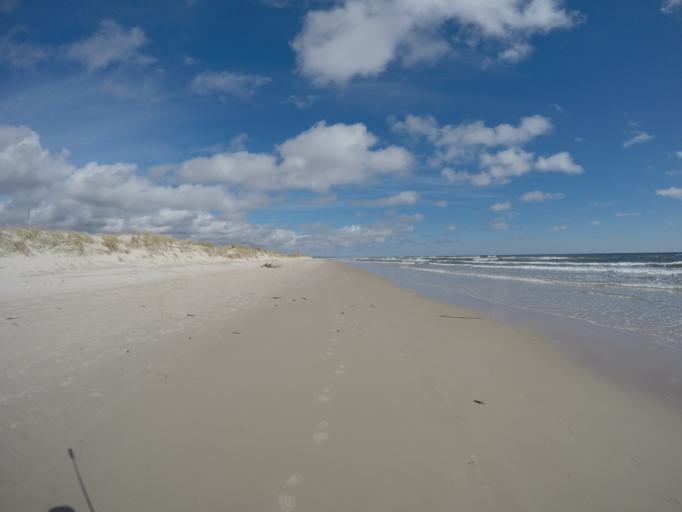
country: SE
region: Skane
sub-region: Simrishamns Kommun
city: Simrishamn
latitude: 55.3917
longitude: 14.2075
